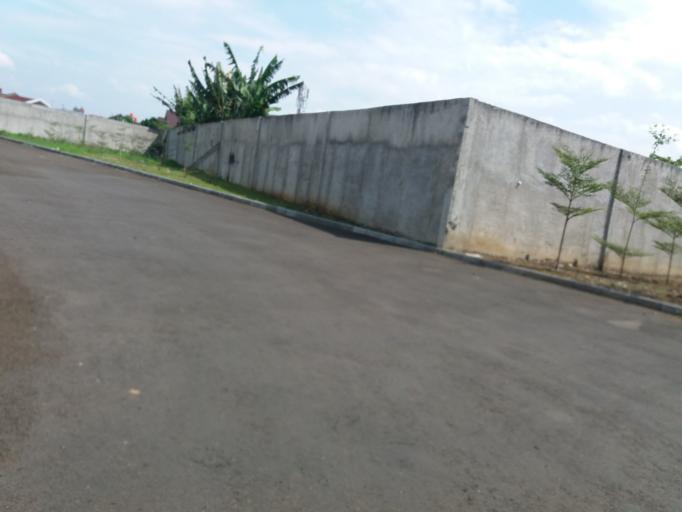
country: ID
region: West Java
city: Bandung
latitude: -6.9209
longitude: 107.6661
